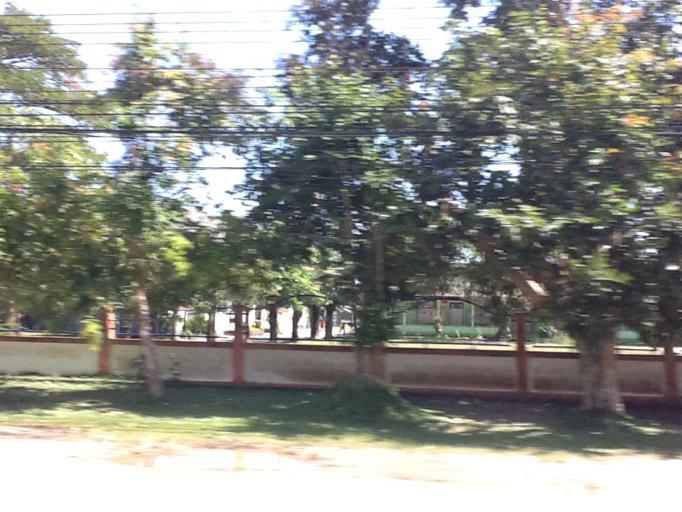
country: TH
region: Phuket
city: Thalang
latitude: 8.0307
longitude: 98.4016
